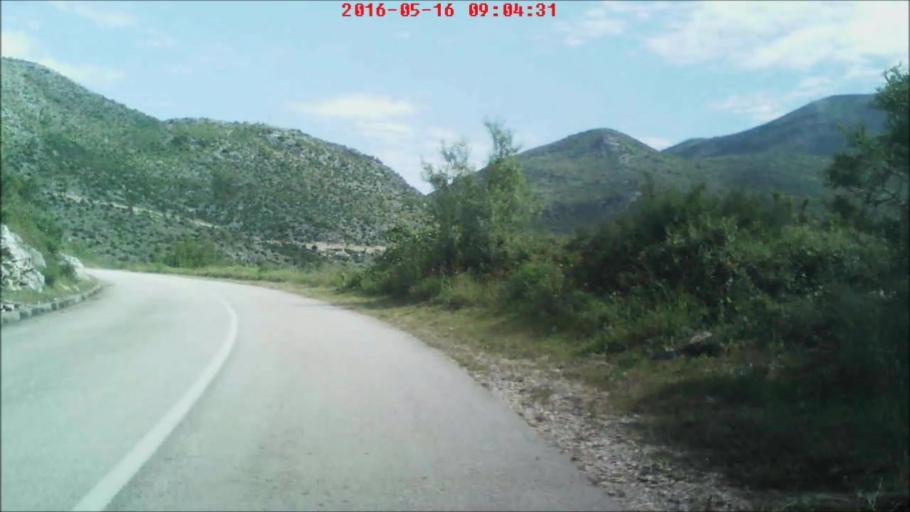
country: HR
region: Dubrovacko-Neretvanska
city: Podgora
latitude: 42.7886
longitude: 17.8735
